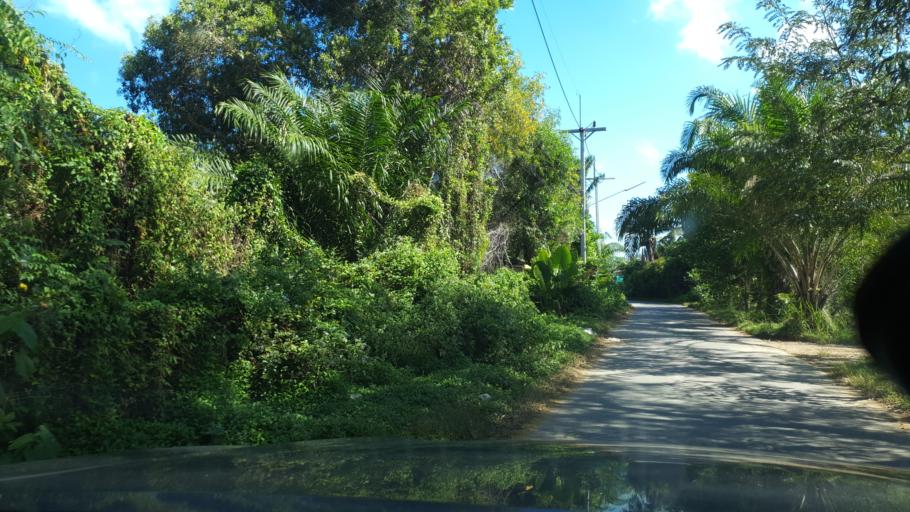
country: TH
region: Krabi
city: Krabi
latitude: 8.0255
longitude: 98.8799
